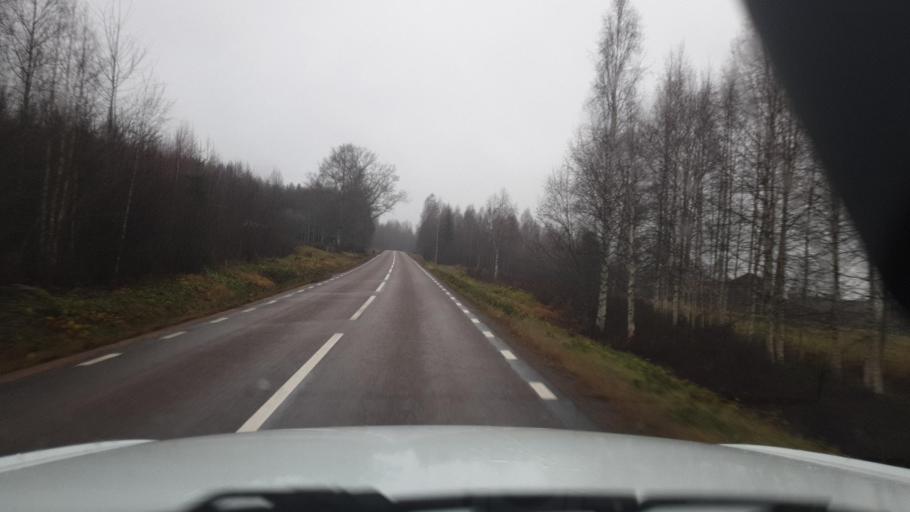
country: SE
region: Vaermland
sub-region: Torsby Kommun
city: Torsby
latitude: 59.9142
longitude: 12.9023
